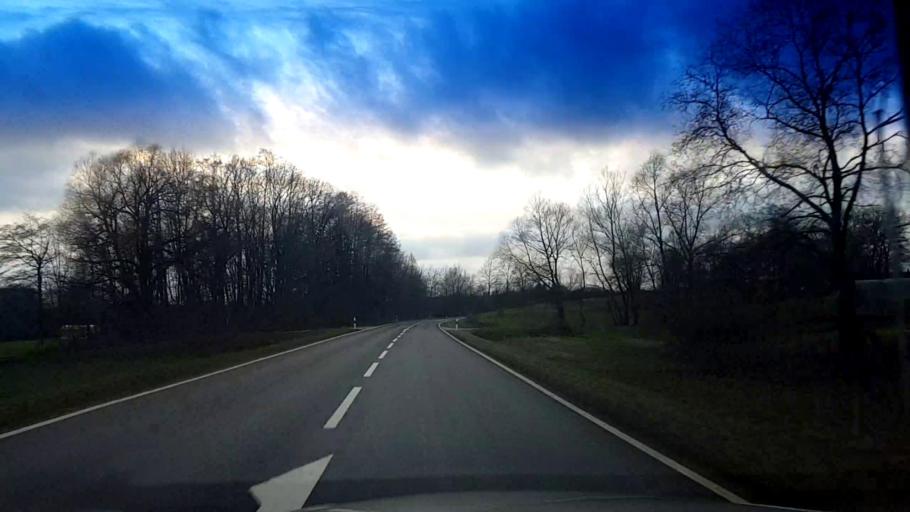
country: DE
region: Bavaria
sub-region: Upper Franconia
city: Litzendorf
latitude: 49.8710
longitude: 11.0332
